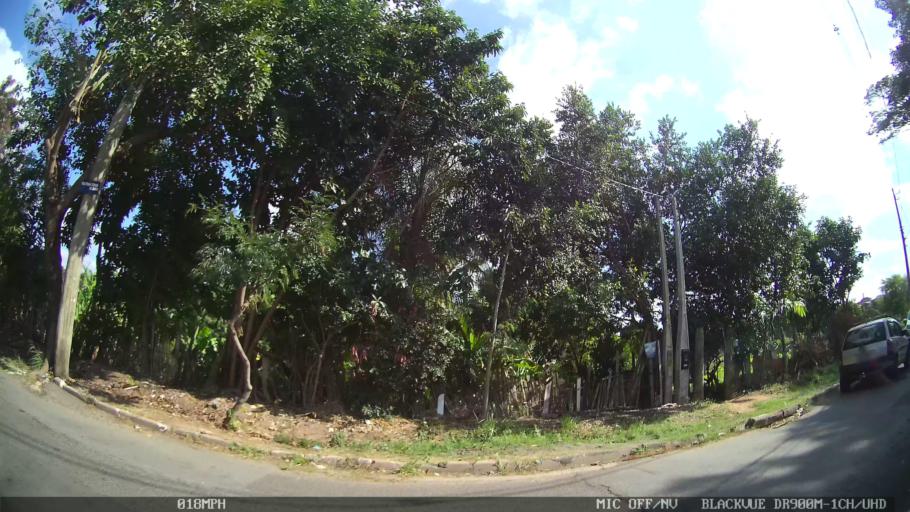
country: BR
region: Sao Paulo
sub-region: Campinas
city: Campinas
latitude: -22.9379
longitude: -47.1226
